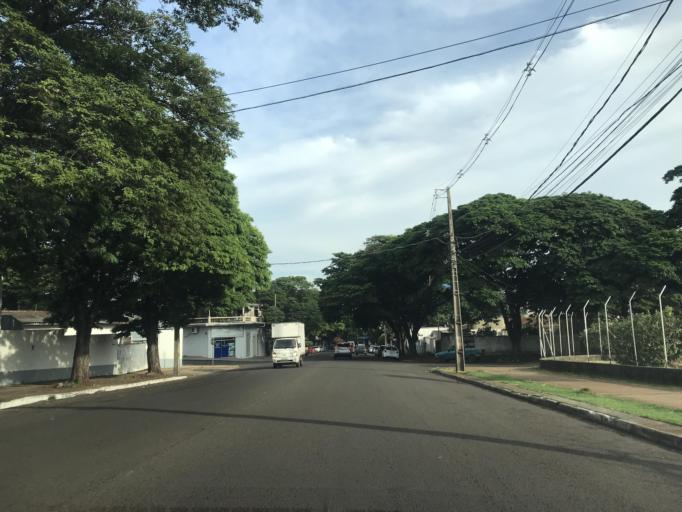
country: BR
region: Parana
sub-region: Maringa
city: Maringa
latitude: -23.4259
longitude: -51.9649
